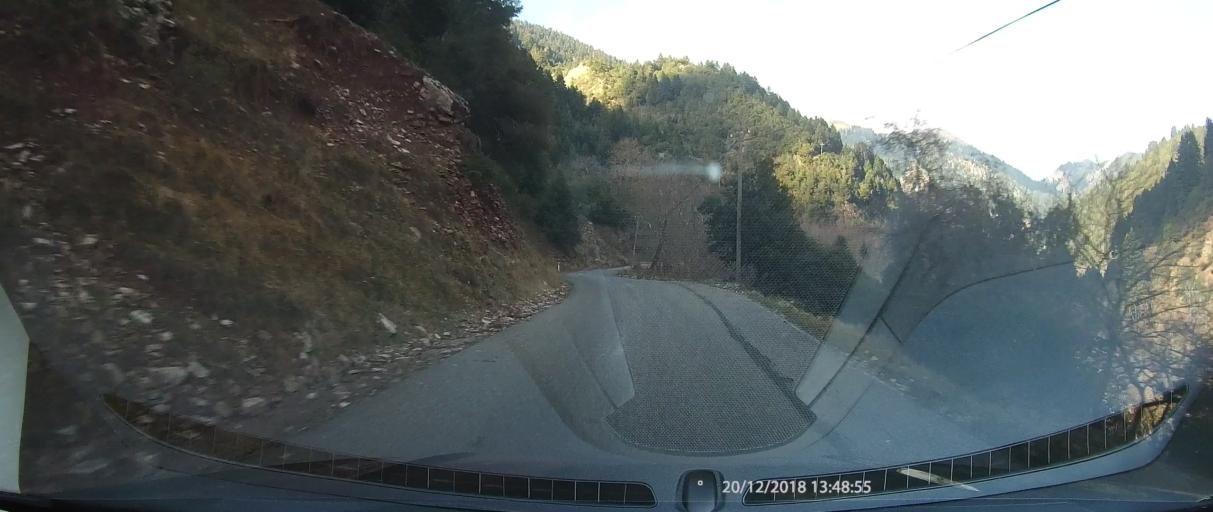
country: GR
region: West Greece
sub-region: Nomos Aitolias kai Akarnanias
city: Paravola
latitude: 38.6888
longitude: 21.6088
